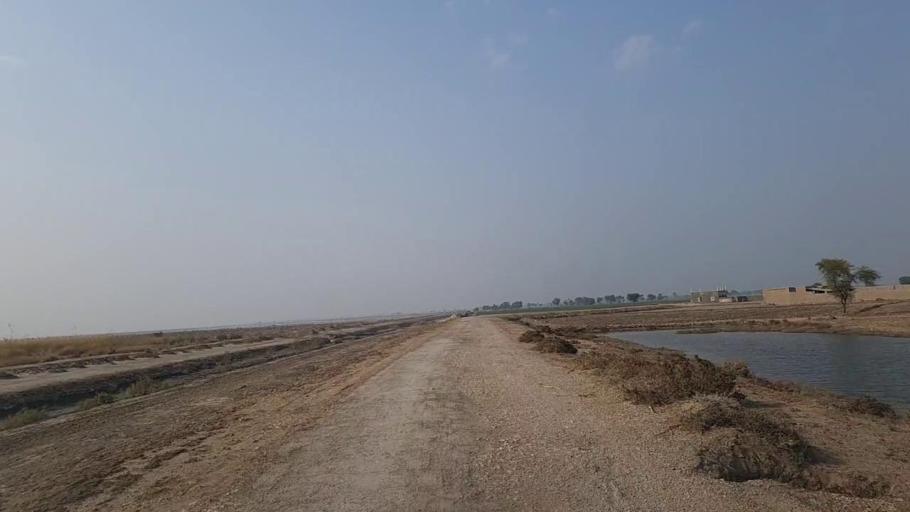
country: PK
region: Sindh
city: Nawabshah
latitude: 26.3332
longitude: 68.4744
